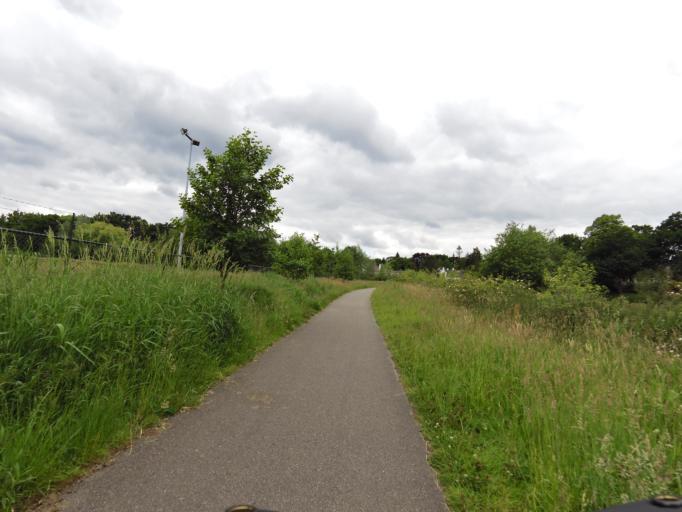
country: NL
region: North Brabant
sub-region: Gemeente Breda
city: Breda
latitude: 51.5652
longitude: 4.7843
